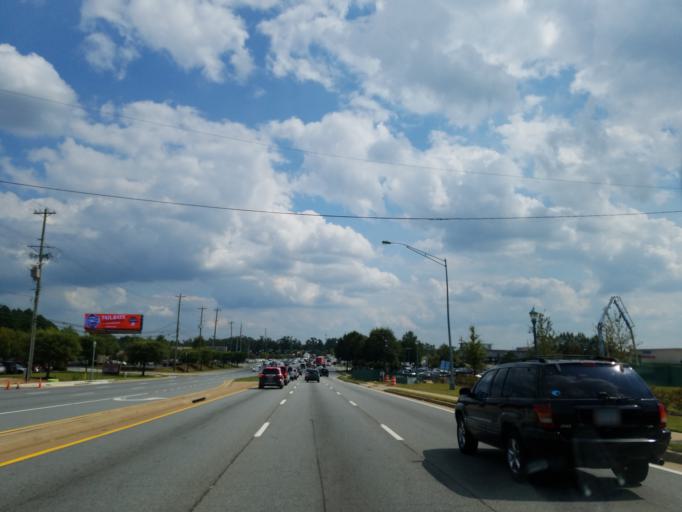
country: US
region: Georgia
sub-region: Gwinnett County
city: Buford
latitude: 34.0803
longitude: -83.9864
